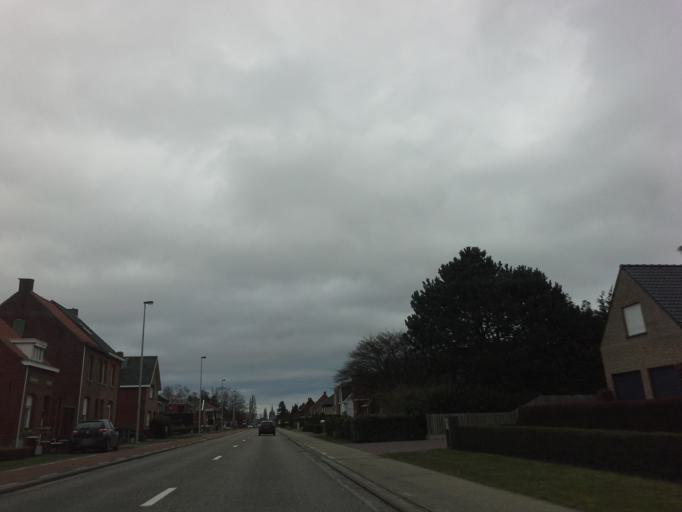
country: BE
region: Flanders
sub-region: Provincie Antwerpen
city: Olen
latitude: 51.1313
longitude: 4.8316
